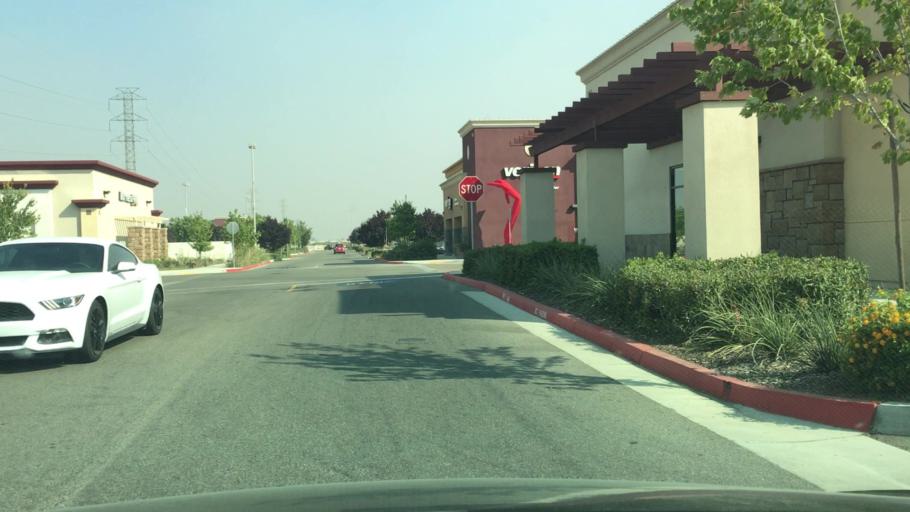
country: US
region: California
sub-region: Fresno County
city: Biola
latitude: 36.8342
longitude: -119.9103
